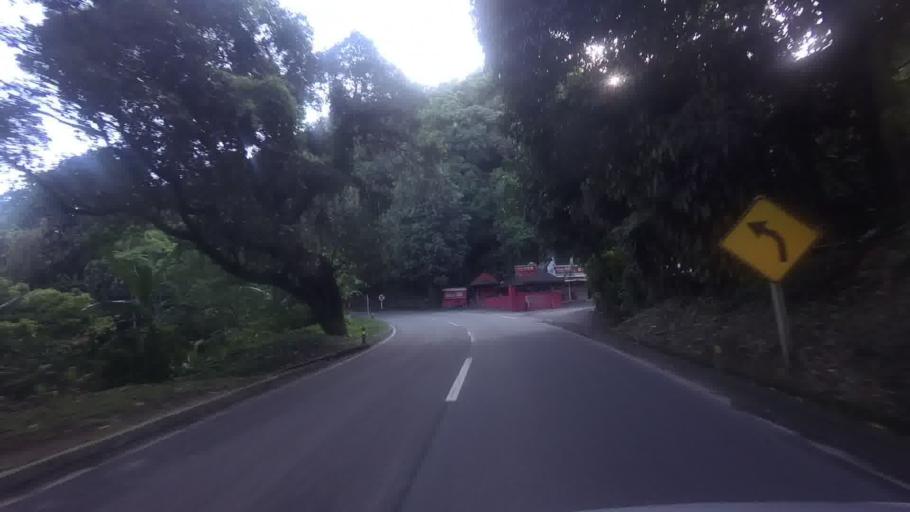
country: BR
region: Rio de Janeiro
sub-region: Petropolis
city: Petropolis
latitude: -22.5778
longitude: -43.2619
